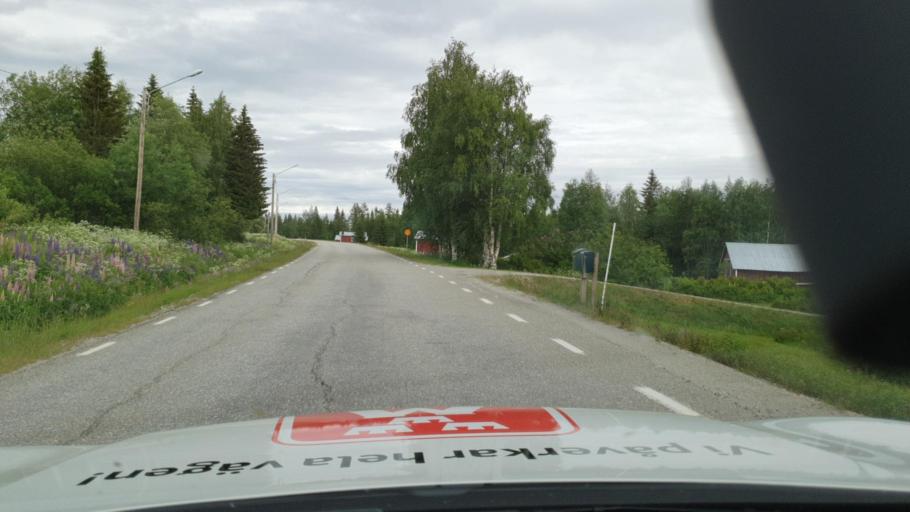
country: SE
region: Vaesterbotten
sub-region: Lycksele Kommun
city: Soderfors
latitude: 64.3608
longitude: 18.1055
